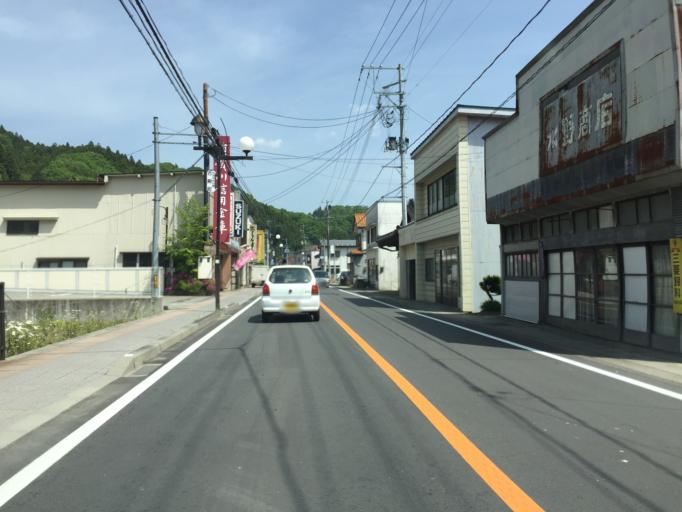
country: JP
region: Fukushima
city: Ishikawa
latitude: 37.0926
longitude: 140.5506
